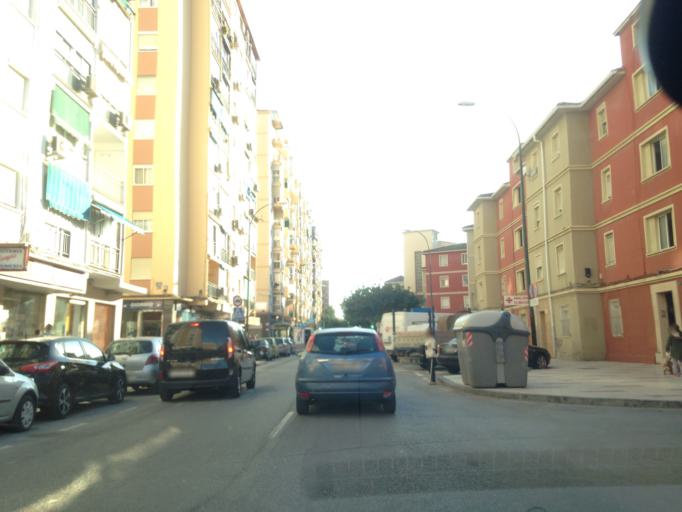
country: ES
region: Andalusia
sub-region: Provincia de Malaga
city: Malaga
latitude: 36.7116
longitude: -4.4417
